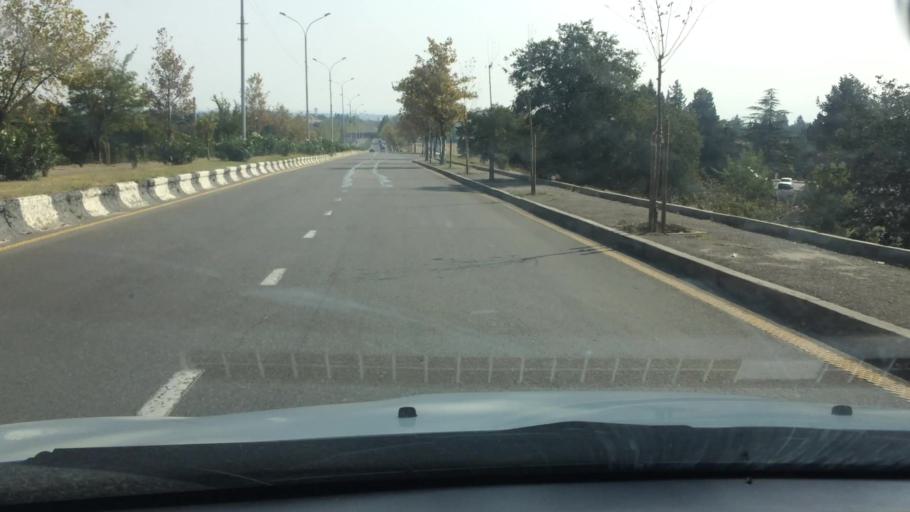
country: GE
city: Didi Lilo
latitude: 41.6845
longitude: 44.9537
